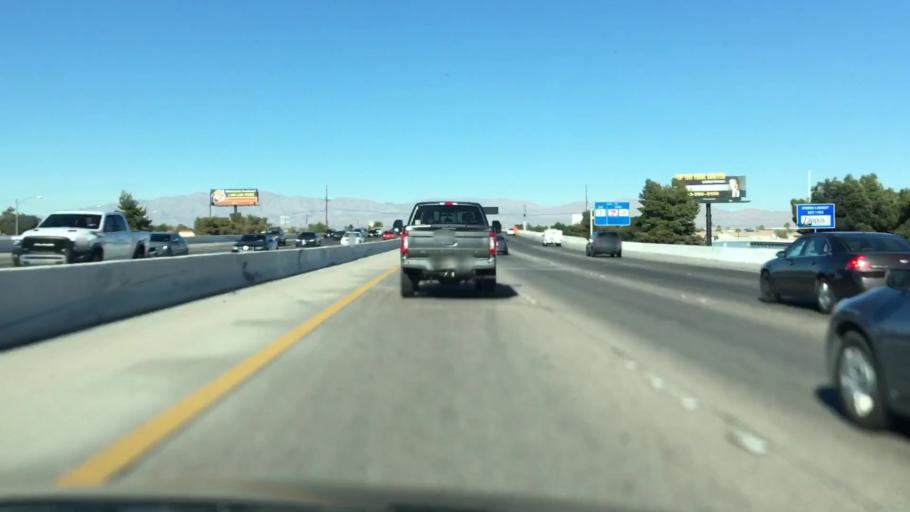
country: US
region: Nevada
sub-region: Clark County
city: Winchester
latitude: 36.1418
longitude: -115.0911
